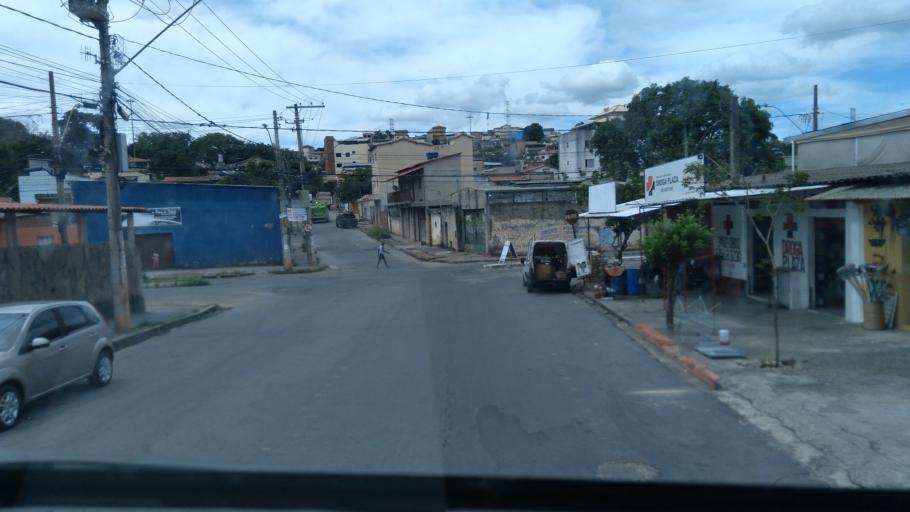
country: BR
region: Minas Gerais
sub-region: Belo Horizonte
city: Belo Horizonte
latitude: -19.8776
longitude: -43.8954
